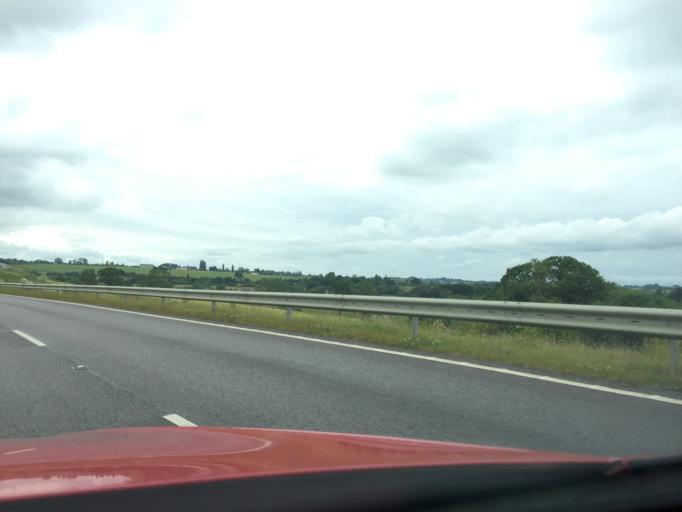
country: GB
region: England
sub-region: Northamptonshire
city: Long Buckby
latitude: 52.2434
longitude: -1.0742
